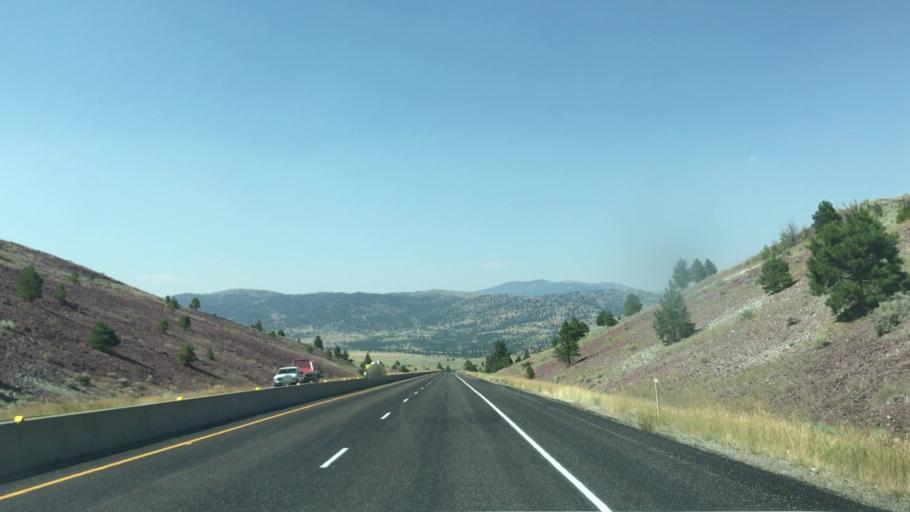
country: US
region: Montana
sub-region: Lewis and Clark County
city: Helena Valley Northwest
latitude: 46.7714
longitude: -112.0326
